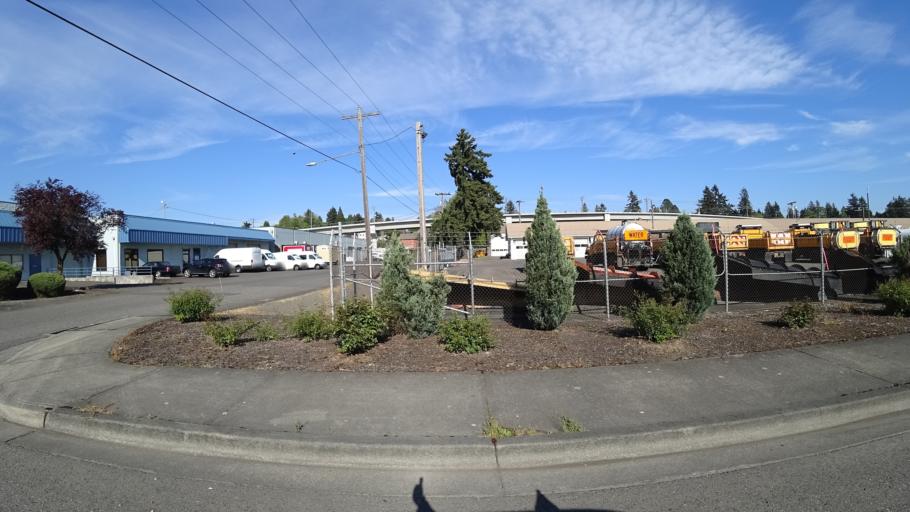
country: US
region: Oregon
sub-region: Clackamas County
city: Milwaukie
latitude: 45.4580
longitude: -122.6381
